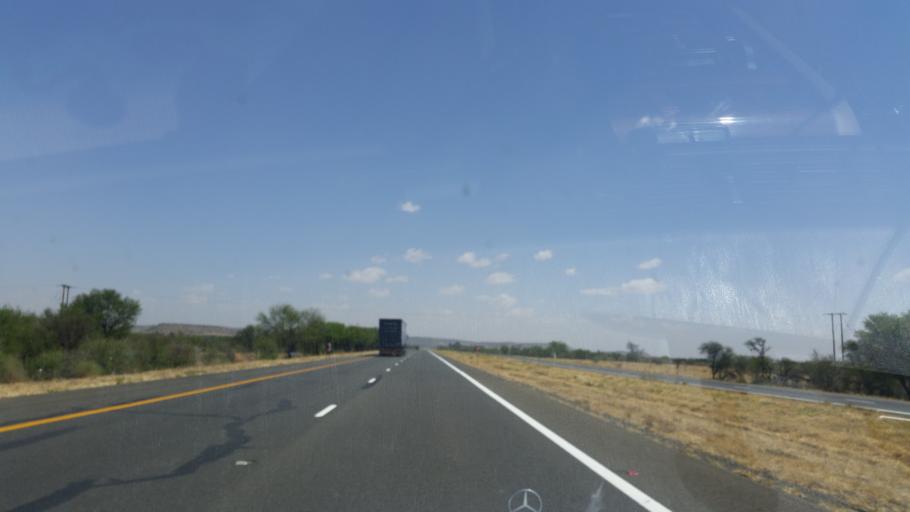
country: ZA
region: Orange Free State
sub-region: Mangaung Metropolitan Municipality
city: Bloemfontein
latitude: -28.9577
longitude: 26.3751
